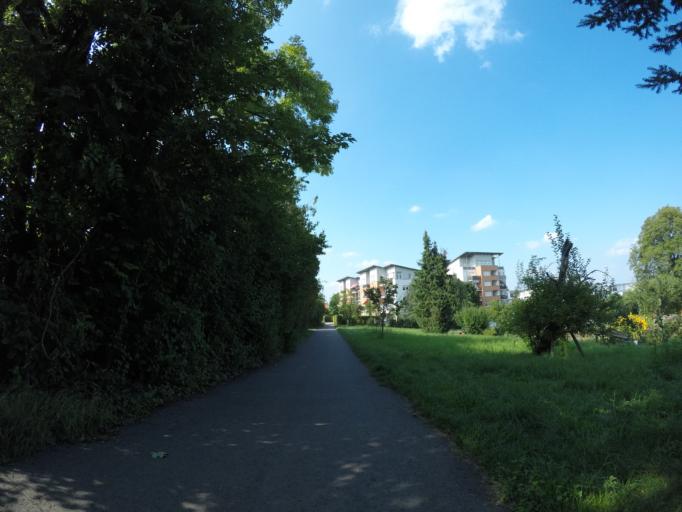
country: DE
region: Baden-Wuerttemberg
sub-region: Tuebingen Region
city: Reutlingen
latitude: 48.4845
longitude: 9.1868
